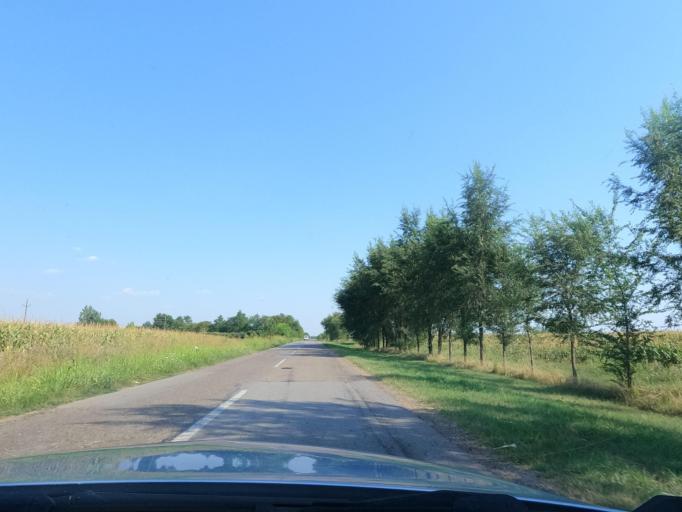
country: RS
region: Autonomna Pokrajina Vojvodina
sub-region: Juznobacki Okrug
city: Becej
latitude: 45.6476
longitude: 19.9821
